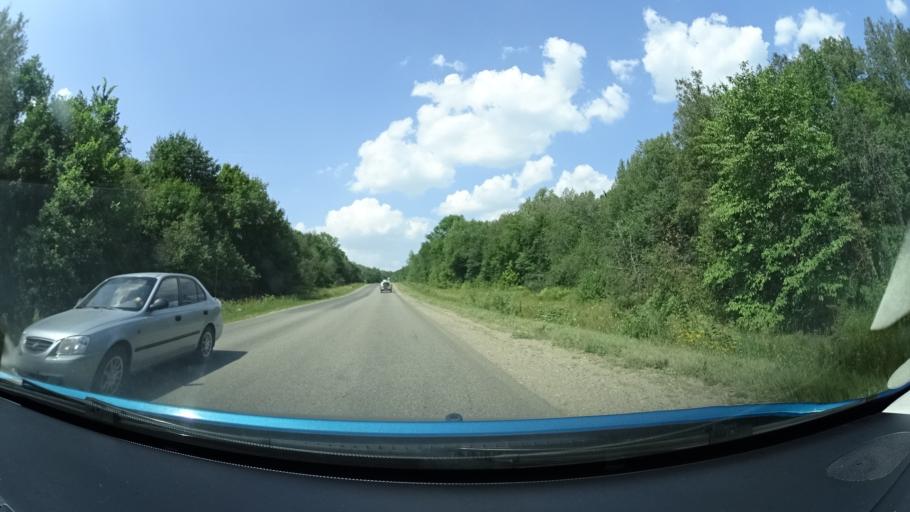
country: RU
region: Bashkortostan
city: Oktyabr'skiy
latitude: 54.4567
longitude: 53.5844
